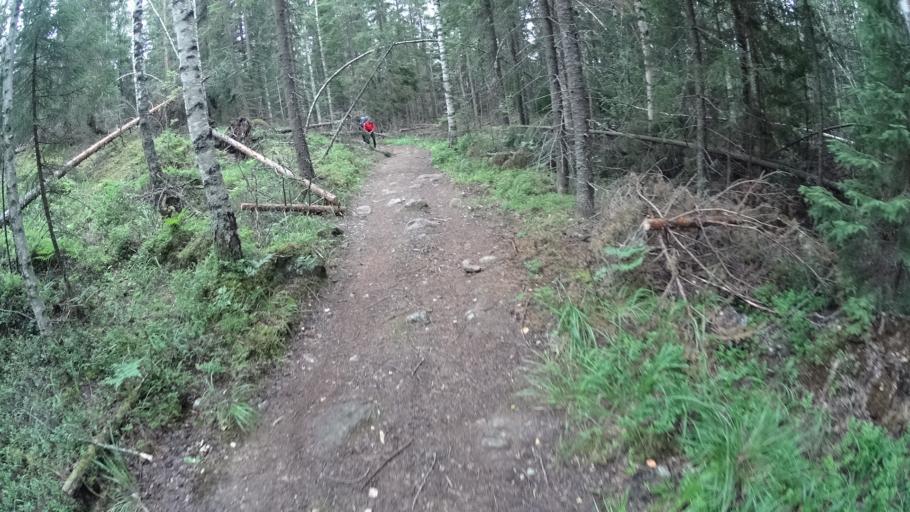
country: FI
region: Southern Savonia
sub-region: Mikkeli
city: Maentyharju
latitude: 61.1818
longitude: 26.8882
